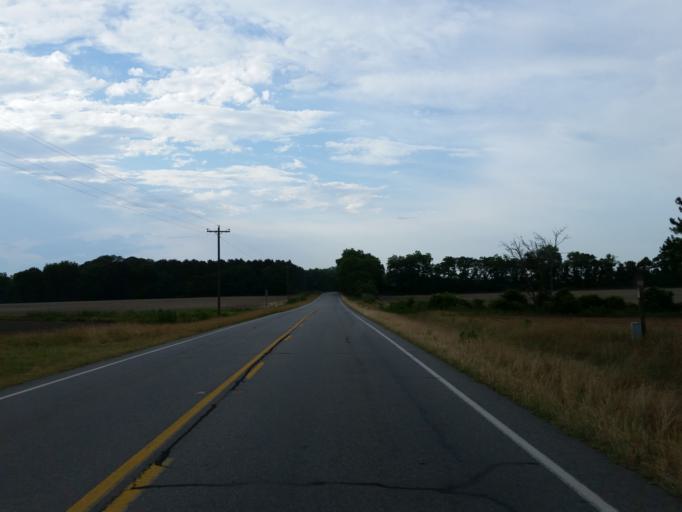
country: US
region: Georgia
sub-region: Dooly County
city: Vienna
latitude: 32.1385
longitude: -83.7969
